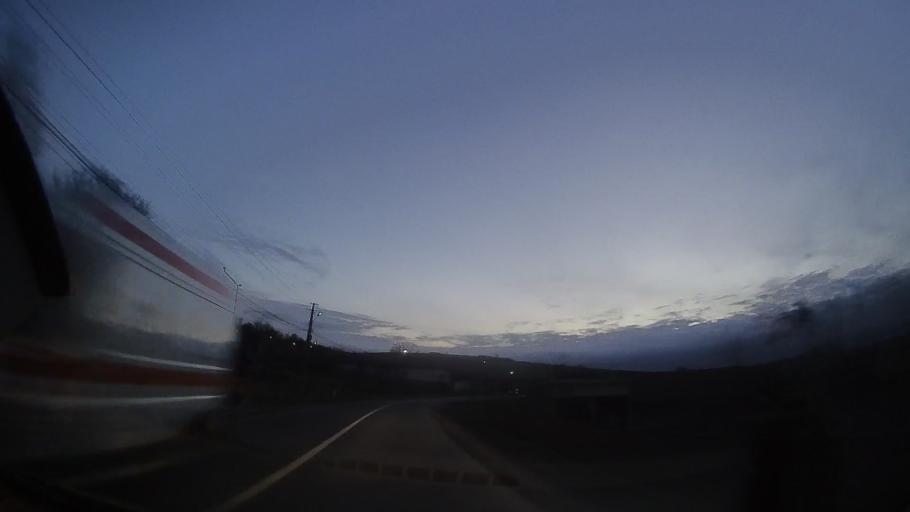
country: RO
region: Mures
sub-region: Comuna Sarmasu
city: Sarmasu
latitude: 46.7622
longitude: 24.1804
